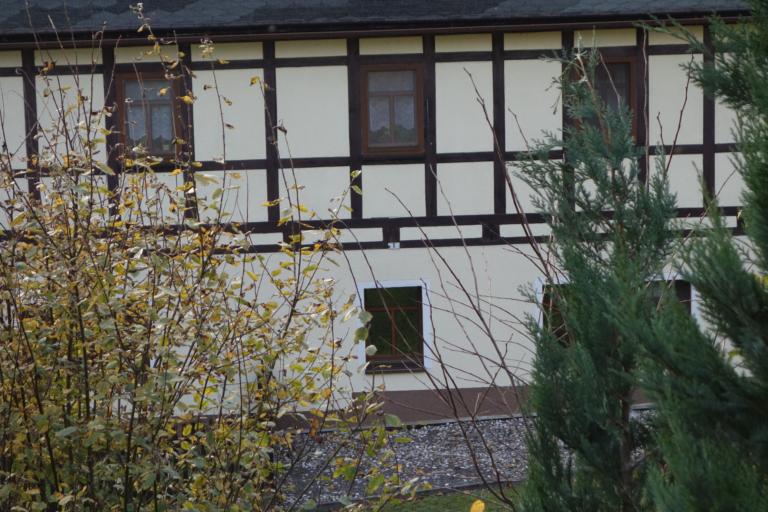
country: DE
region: Saxony
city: Olbernhau
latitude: 50.6516
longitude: 13.3699
